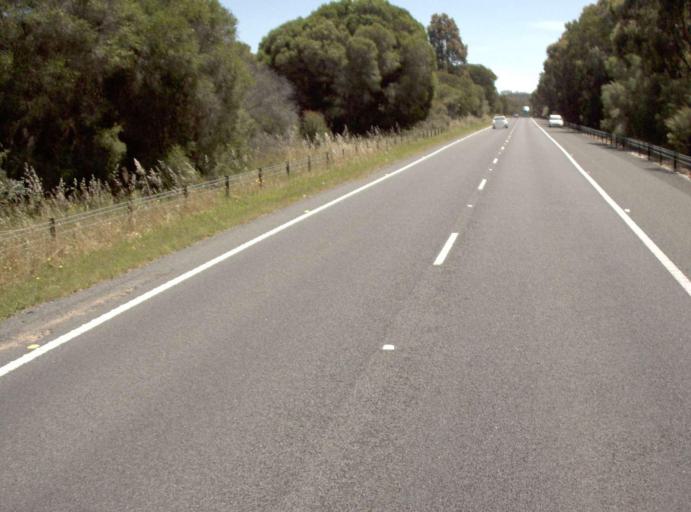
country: AU
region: Victoria
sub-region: Latrobe
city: Morwell
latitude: -38.2229
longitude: 146.3405
